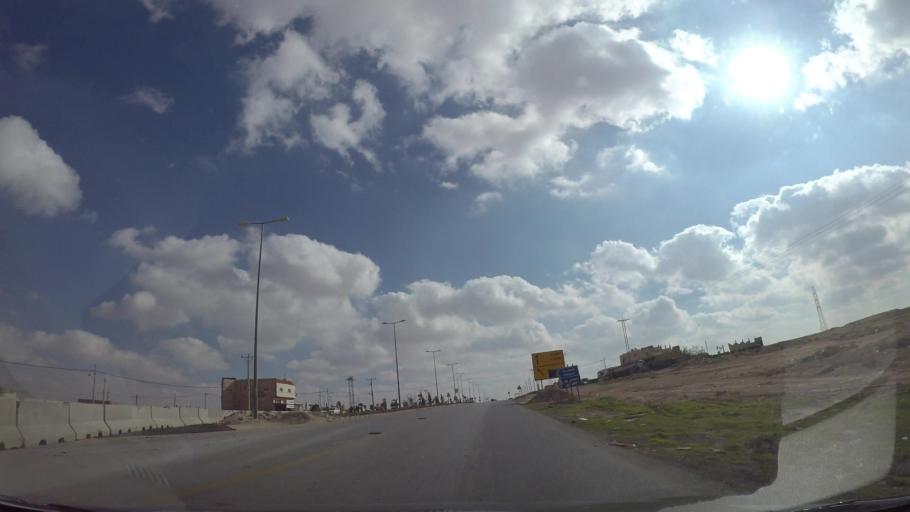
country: JO
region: Amman
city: Al Jizah
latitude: 31.6091
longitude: 35.9999
